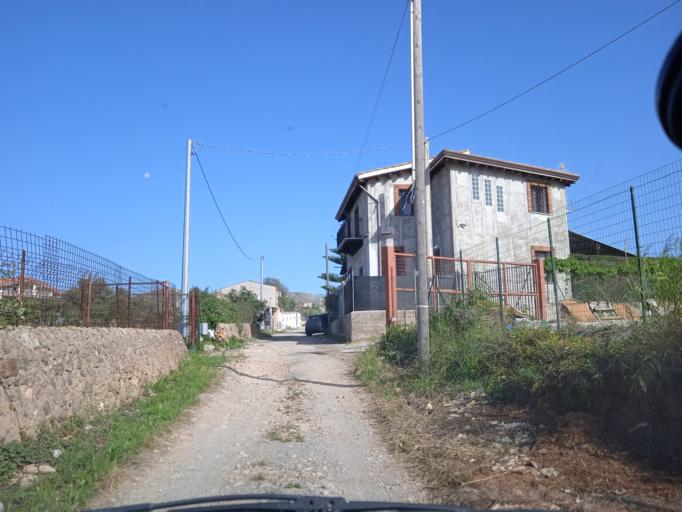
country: IT
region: Sicily
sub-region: Palermo
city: Villabate
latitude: 38.0815
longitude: 13.4524
